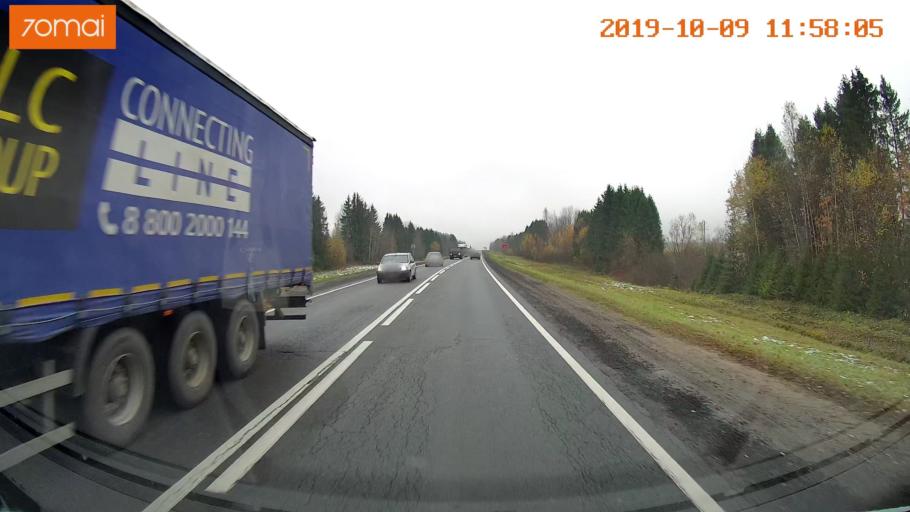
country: RU
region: Vologda
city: Gryazovets
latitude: 58.7232
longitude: 40.2960
